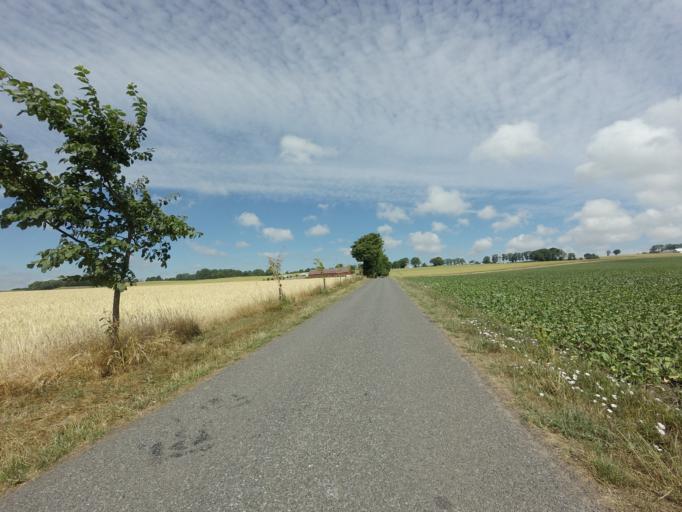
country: SE
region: Skane
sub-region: Simrishamns Kommun
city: Simrishamn
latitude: 55.4889
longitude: 14.3107
